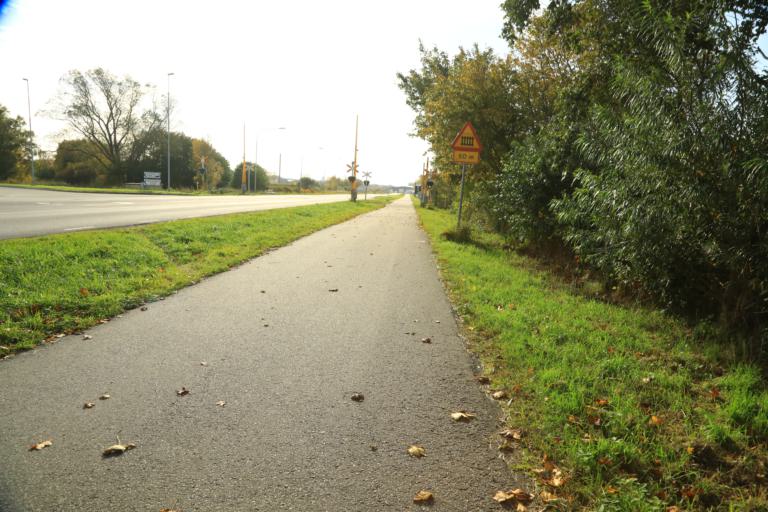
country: SE
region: Halland
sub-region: Varbergs Kommun
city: Varberg
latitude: 57.1210
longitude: 12.2494
